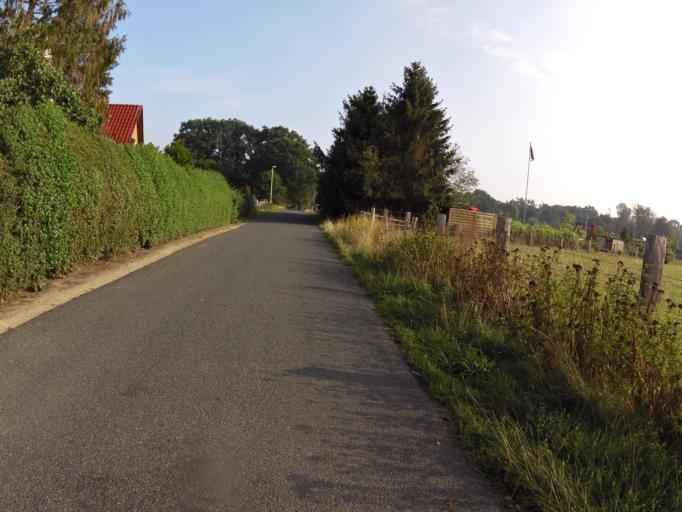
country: DE
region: Lower Saxony
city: Verden
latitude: 52.9396
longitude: 9.2268
